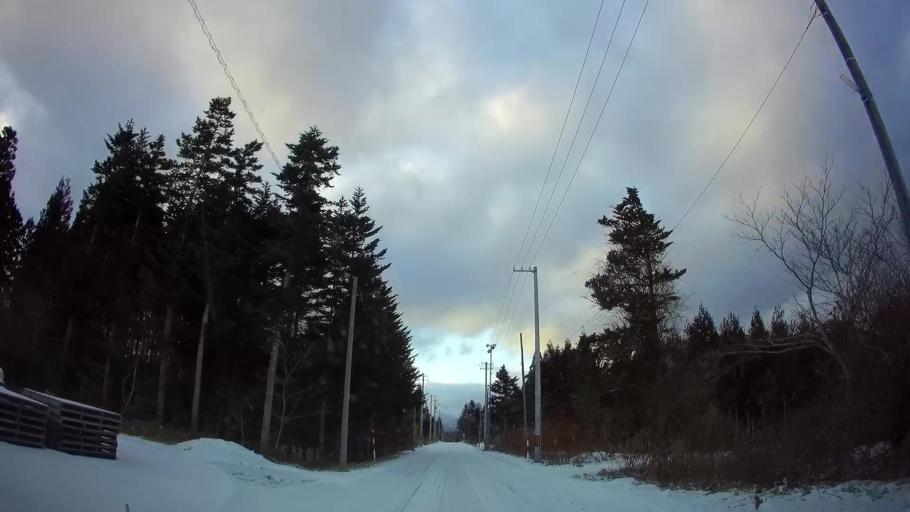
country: JP
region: Hokkaido
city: Nanae
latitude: 42.0210
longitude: 140.8378
